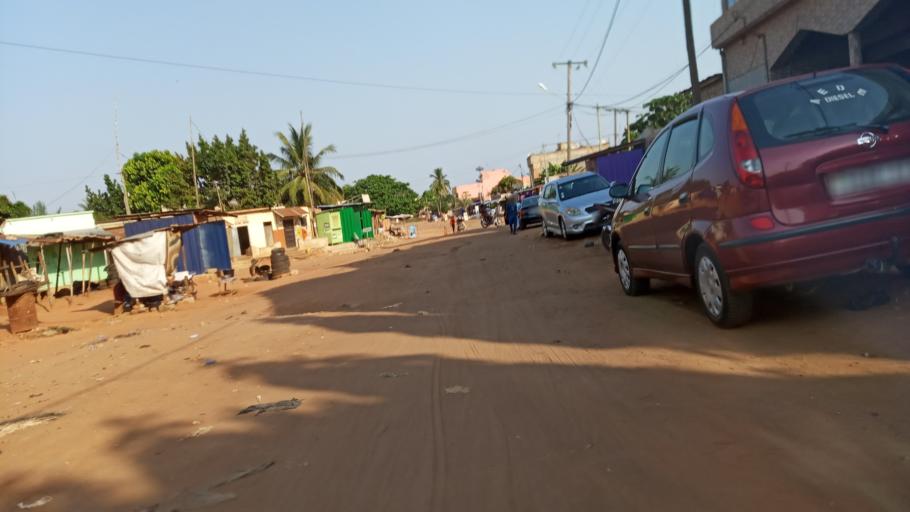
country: TG
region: Maritime
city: Lome
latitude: 6.1807
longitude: 1.1591
